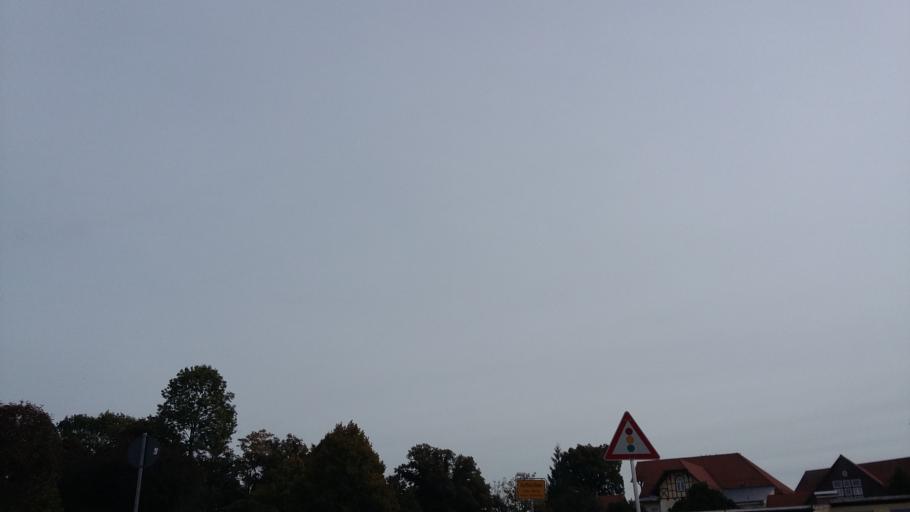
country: DE
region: Bavaria
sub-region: Upper Bavaria
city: Berg
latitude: 47.9580
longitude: 11.3623
